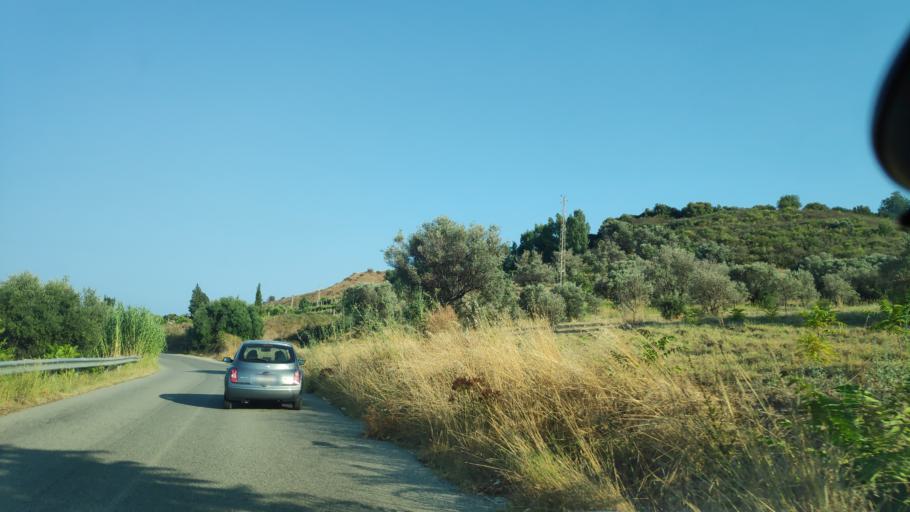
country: IT
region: Calabria
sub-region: Provincia di Reggio Calabria
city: Monasterace Marina
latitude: 38.4508
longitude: 16.5685
